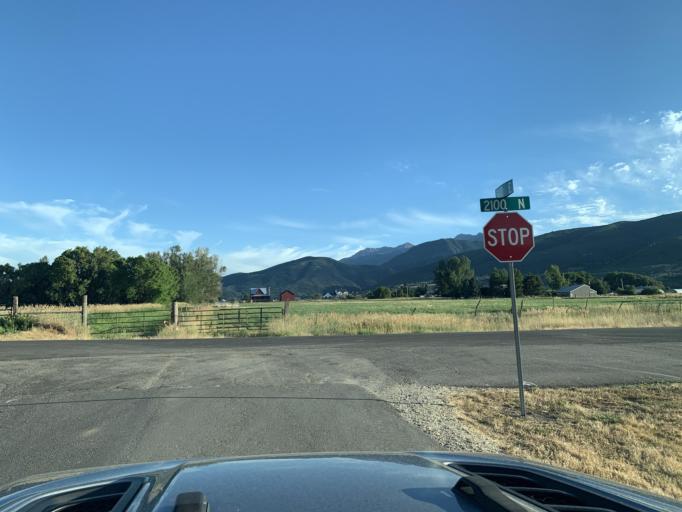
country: US
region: Utah
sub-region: Weber County
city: Wolf Creek
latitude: 41.2971
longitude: -111.8130
